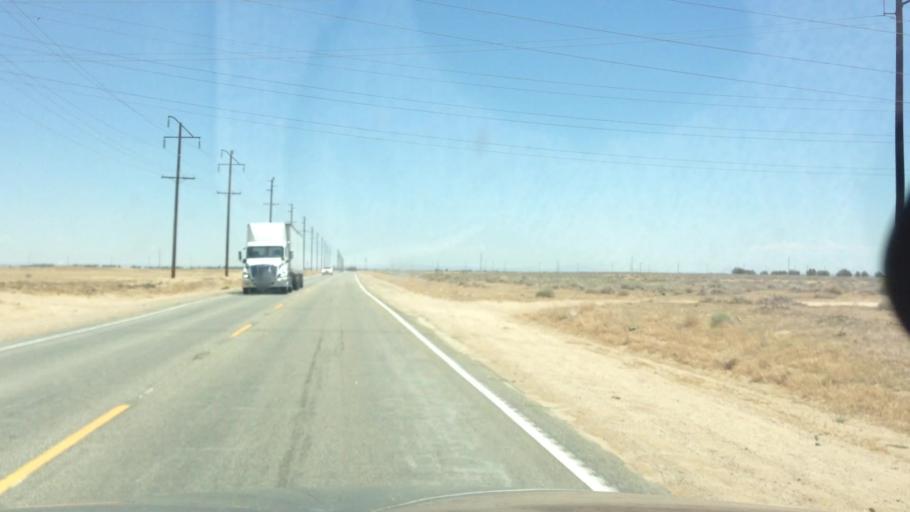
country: US
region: California
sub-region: Los Angeles County
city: Leona Valley
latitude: 34.7759
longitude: -118.3432
